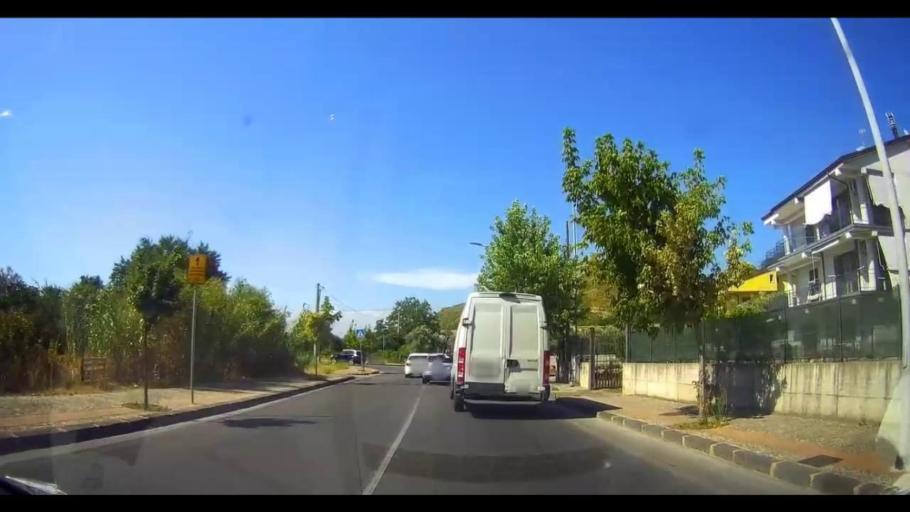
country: IT
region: Calabria
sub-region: Provincia di Cosenza
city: Cosenza
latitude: 39.2993
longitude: 16.2628
